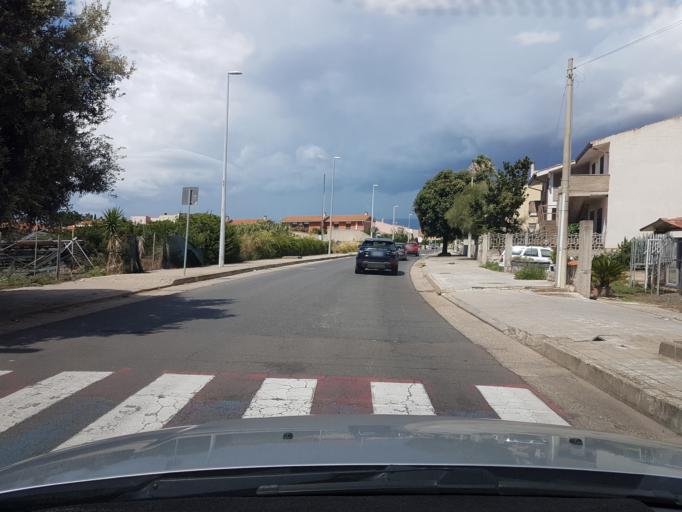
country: IT
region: Sardinia
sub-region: Provincia di Oristano
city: Riola Sardo
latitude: 39.9884
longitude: 8.5409
